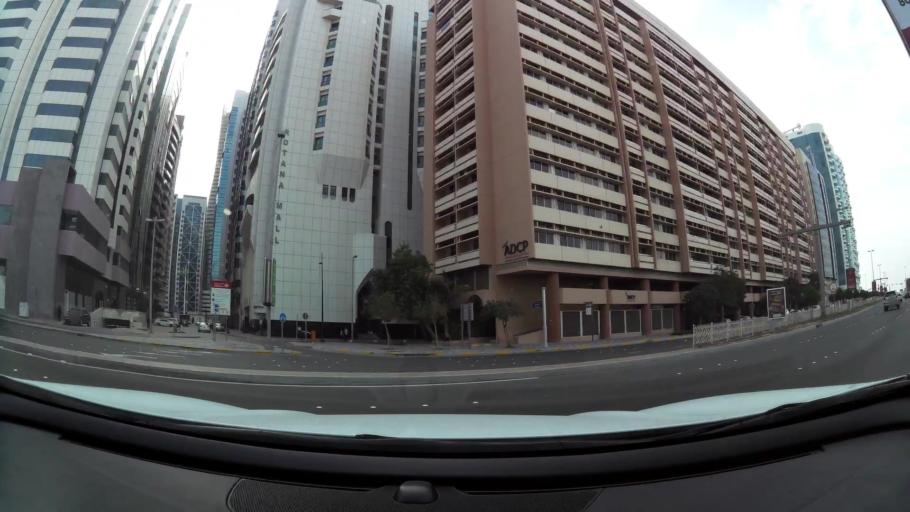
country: AE
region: Abu Dhabi
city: Abu Dhabi
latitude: 24.4709
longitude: 54.3430
